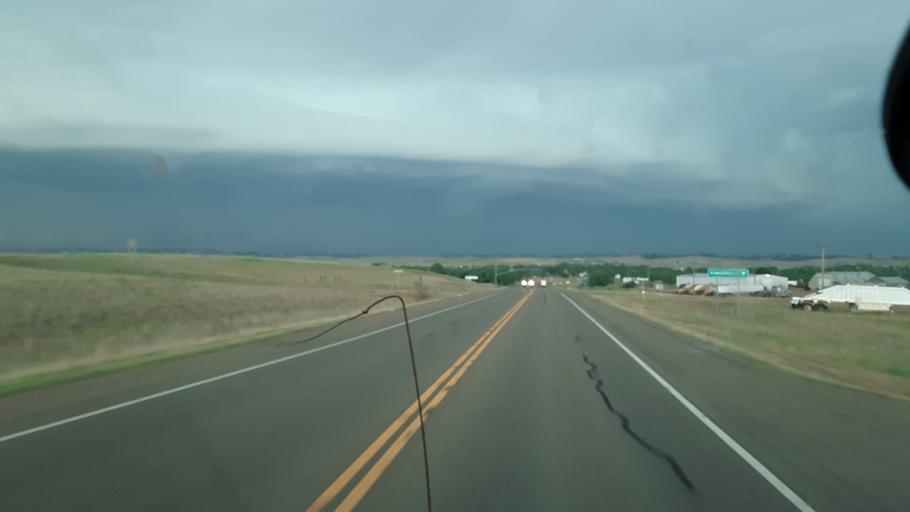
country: US
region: Montana
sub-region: Powder River County
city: Broadus
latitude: 45.4244
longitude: -105.3991
